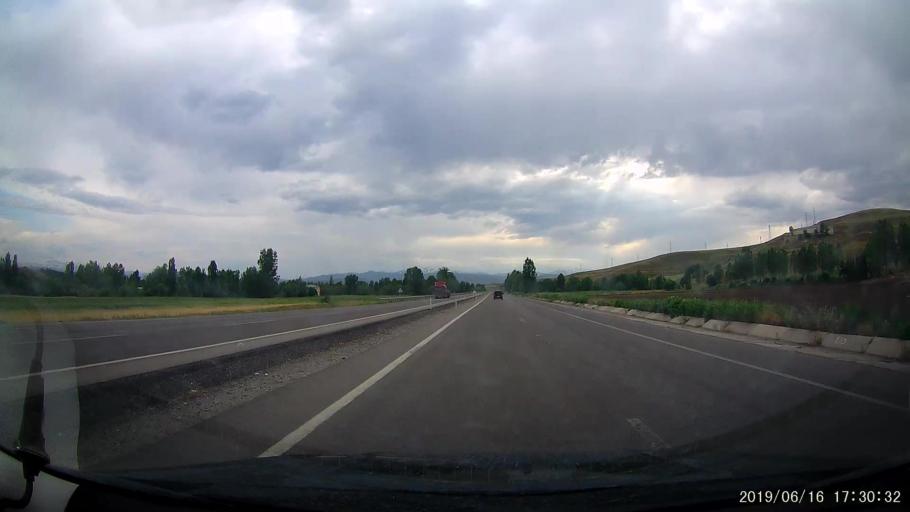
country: TR
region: Erzincan
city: Tercan
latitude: 39.7761
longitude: 40.3446
